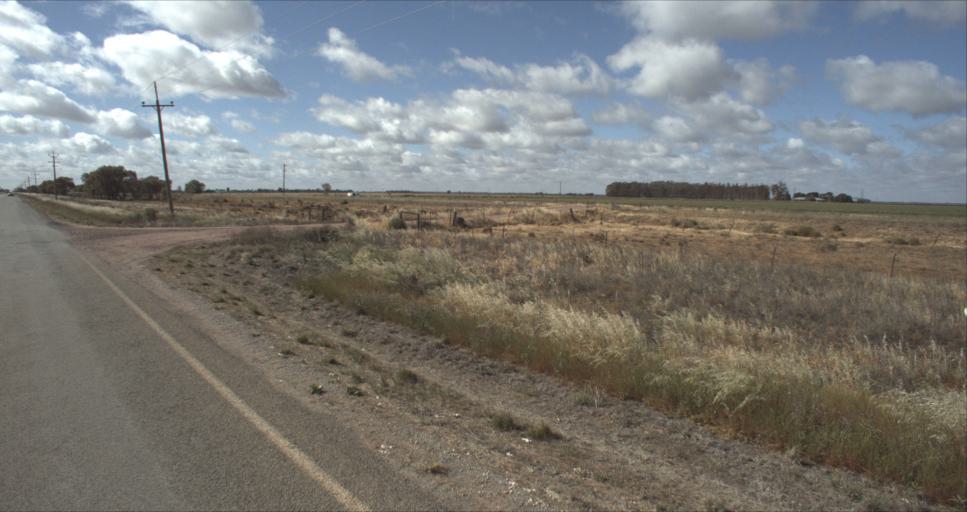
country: AU
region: New South Wales
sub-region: Leeton
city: Leeton
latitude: -34.5285
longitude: 146.2146
